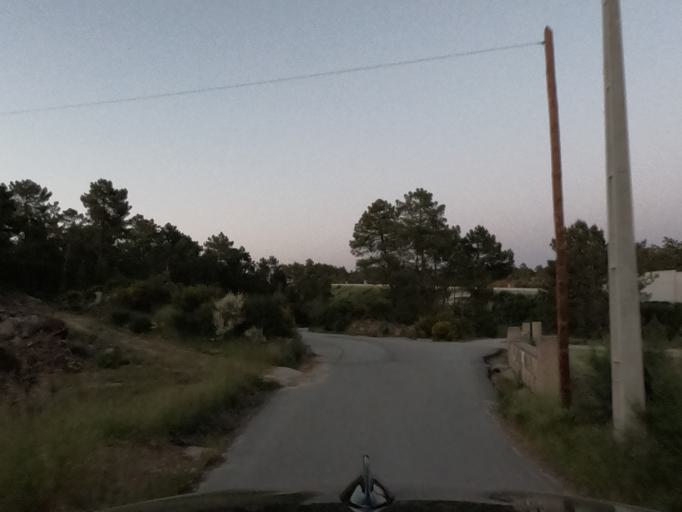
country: PT
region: Vila Real
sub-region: Vila Real
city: Vila Real
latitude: 41.2973
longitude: -7.6865
